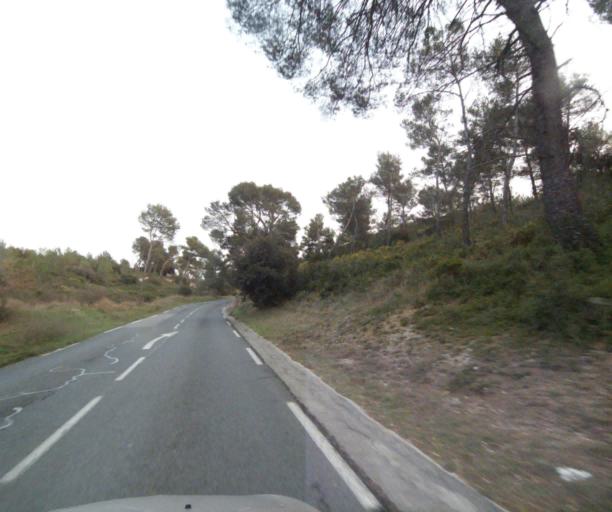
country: FR
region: Provence-Alpes-Cote d'Azur
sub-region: Departement des Bouches-du-Rhone
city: Cabries
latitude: 43.4332
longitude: 5.3656
